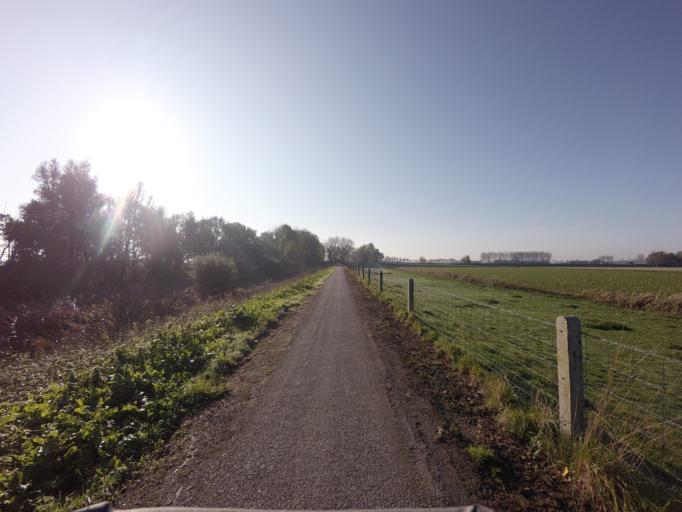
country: NL
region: North Brabant
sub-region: Gemeente Werkendam
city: Werkendam
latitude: 51.7979
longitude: 4.9153
